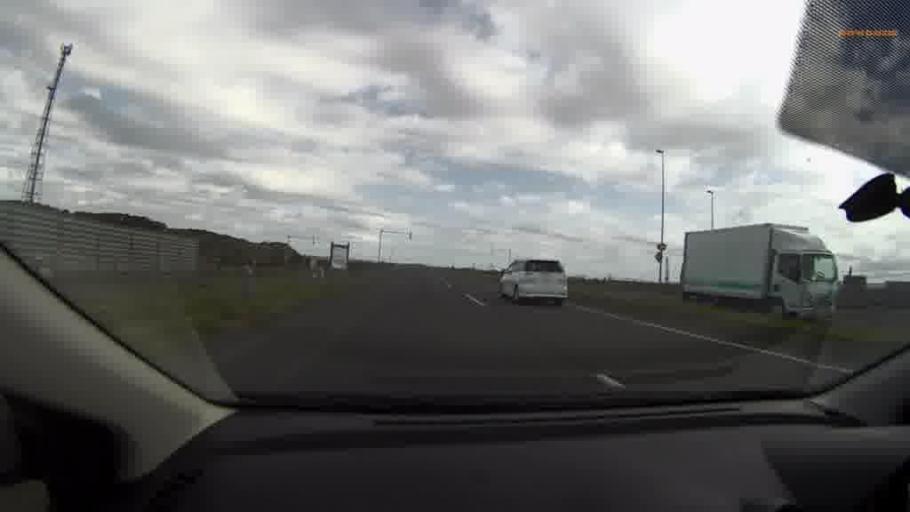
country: JP
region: Hokkaido
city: Kushiro
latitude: 43.0068
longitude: 144.2555
